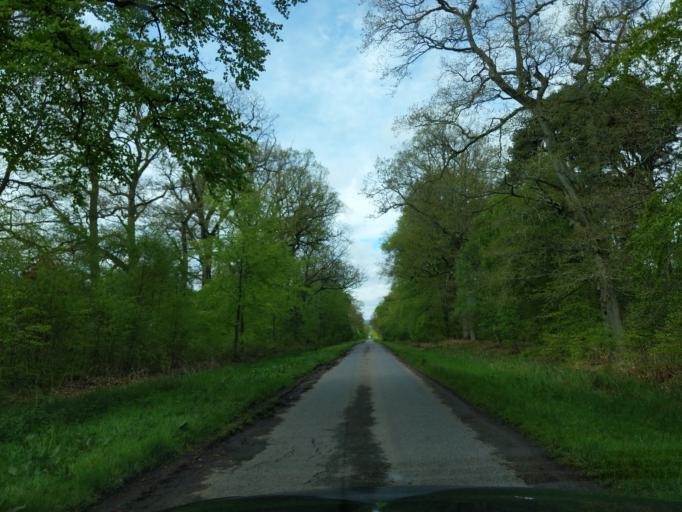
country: GB
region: Scotland
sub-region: The Scottish Borders
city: Saint Boswells
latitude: 55.6427
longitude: -2.5724
